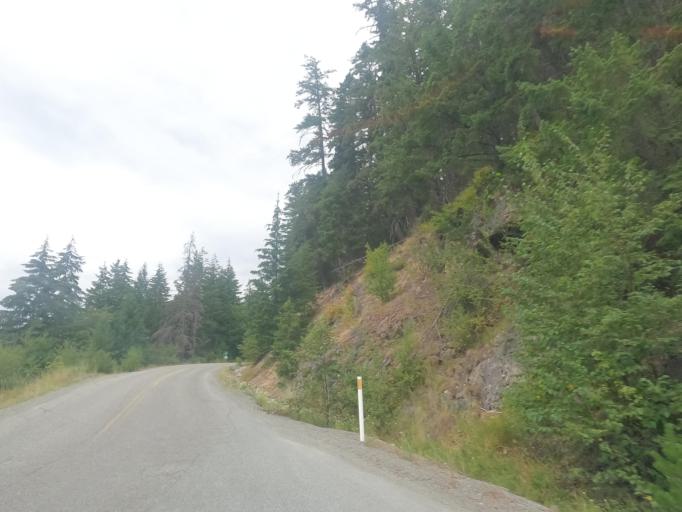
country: CA
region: British Columbia
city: Pemberton
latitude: 50.3002
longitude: -122.5828
